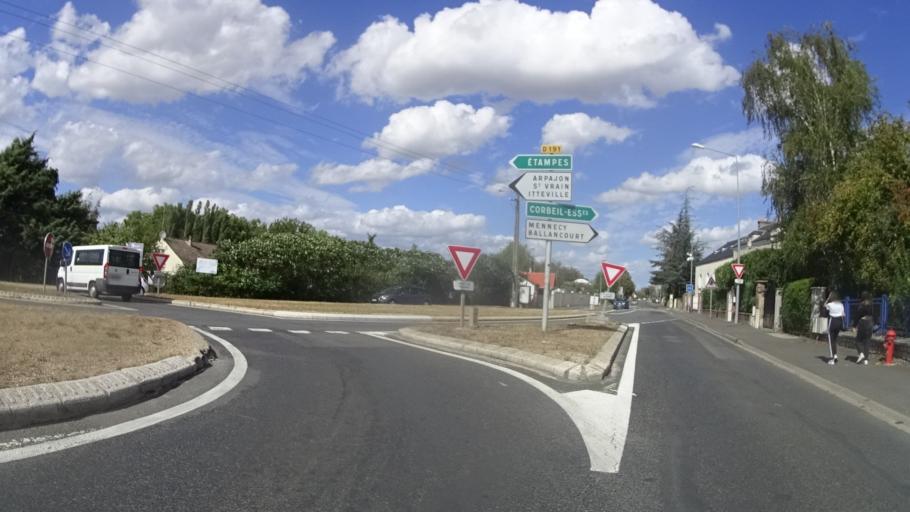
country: FR
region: Ile-de-France
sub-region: Departement de l'Essonne
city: La Ferte-Alais
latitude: 48.4887
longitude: 2.3543
